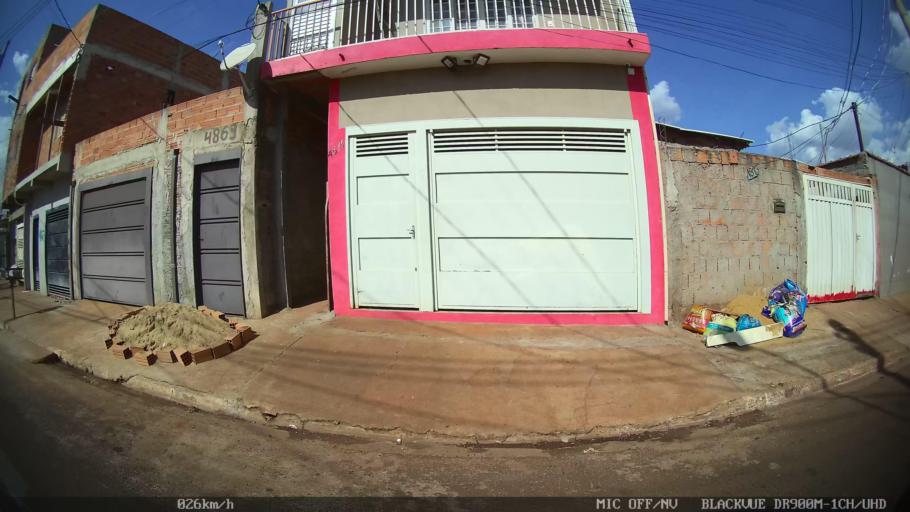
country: BR
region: Sao Paulo
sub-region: Ribeirao Preto
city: Ribeirao Preto
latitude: -21.2012
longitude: -47.8576
